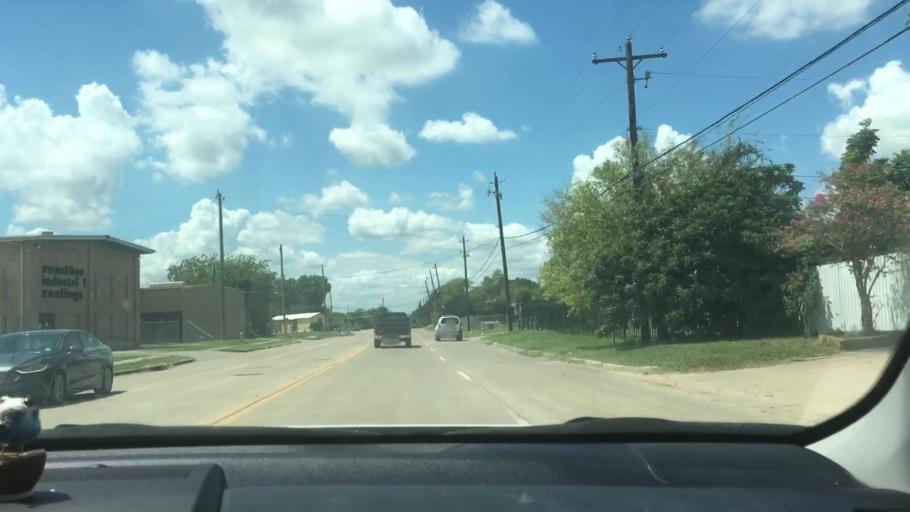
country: US
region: Texas
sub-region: Fort Bend County
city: Fifth Street
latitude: 29.5963
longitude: -95.5581
